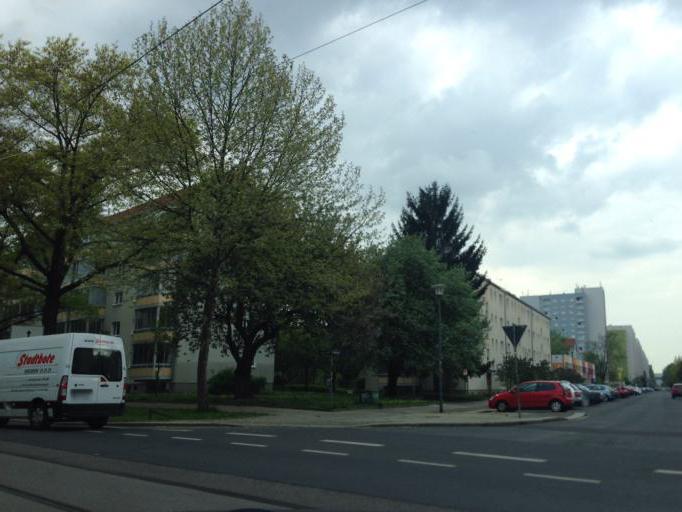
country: DE
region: Saxony
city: Albertstadt
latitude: 51.0487
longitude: 13.7737
